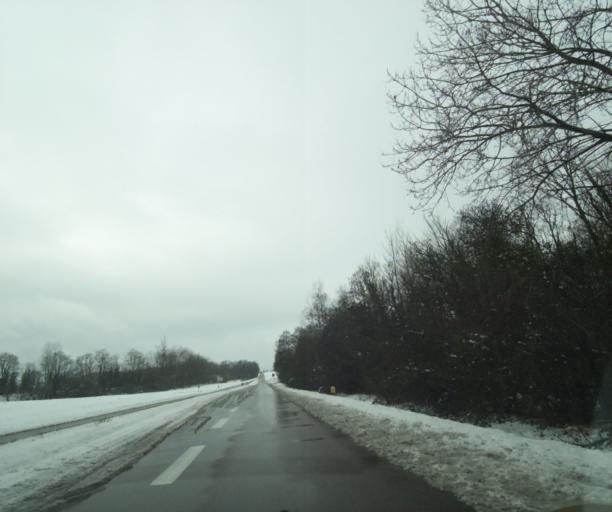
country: FR
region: Champagne-Ardenne
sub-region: Departement de la Haute-Marne
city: Montier-en-Der
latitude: 48.4289
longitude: 4.6760
